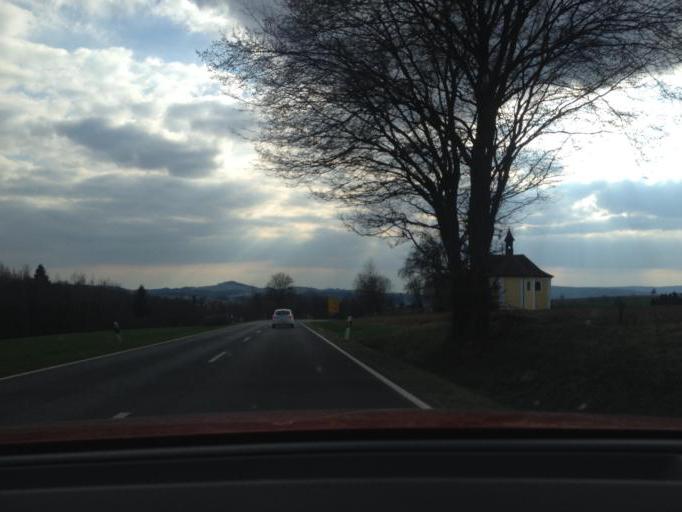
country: DE
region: Bavaria
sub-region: Upper Palatinate
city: Pullenreuth
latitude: 49.9393
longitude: 12.0095
